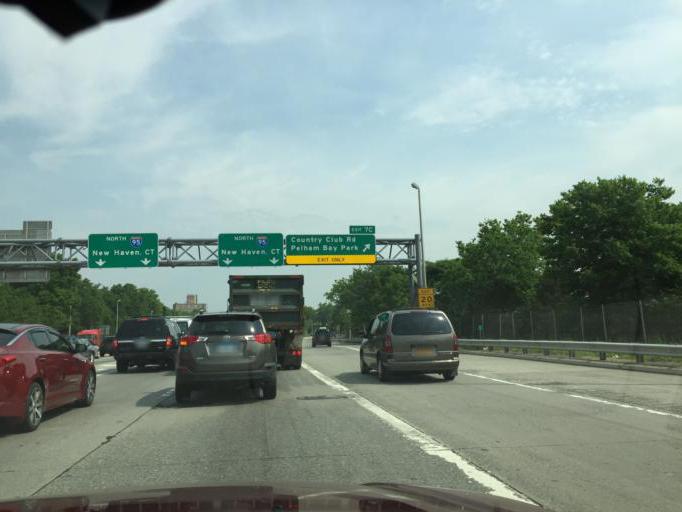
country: US
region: New York
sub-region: Bronx
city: The Bronx
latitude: 40.8402
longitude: -73.8254
